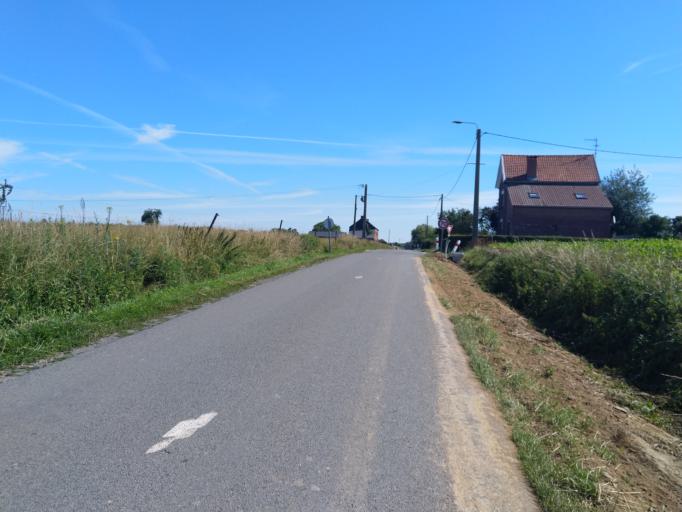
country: FR
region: Nord-Pas-de-Calais
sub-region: Departement du Nord
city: La Longueville
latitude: 50.3412
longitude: 3.8484
